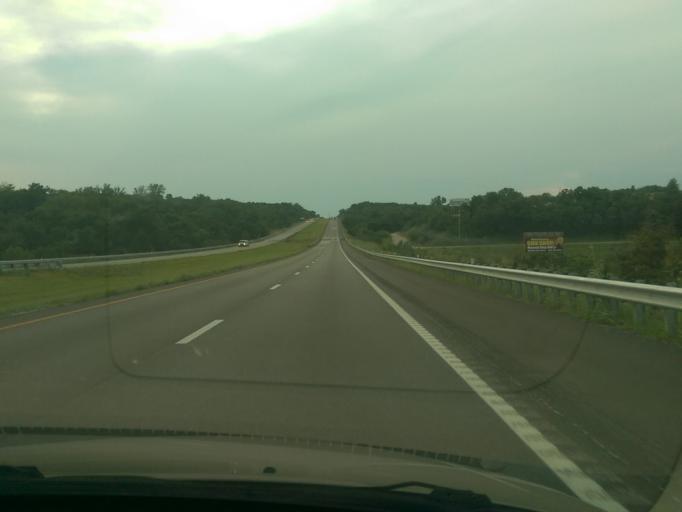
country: US
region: Missouri
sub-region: Andrew County
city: Savannah
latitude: 39.9023
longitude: -94.8821
